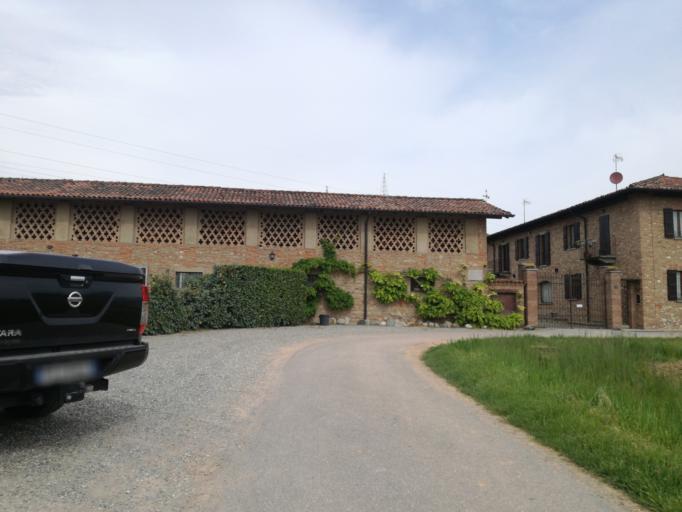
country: IT
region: Lombardy
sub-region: Provincia di Lecco
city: Verderio Superiore
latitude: 45.6507
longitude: 9.4517
